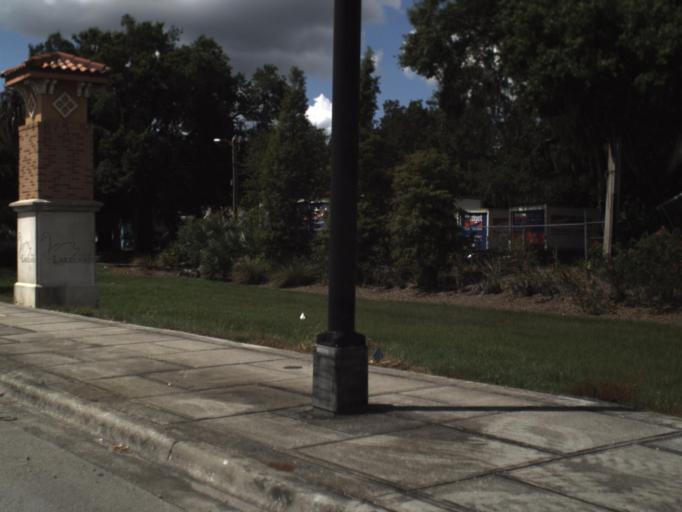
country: US
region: Florida
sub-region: Polk County
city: Lakeland
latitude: 28.0547
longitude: -81.9576
